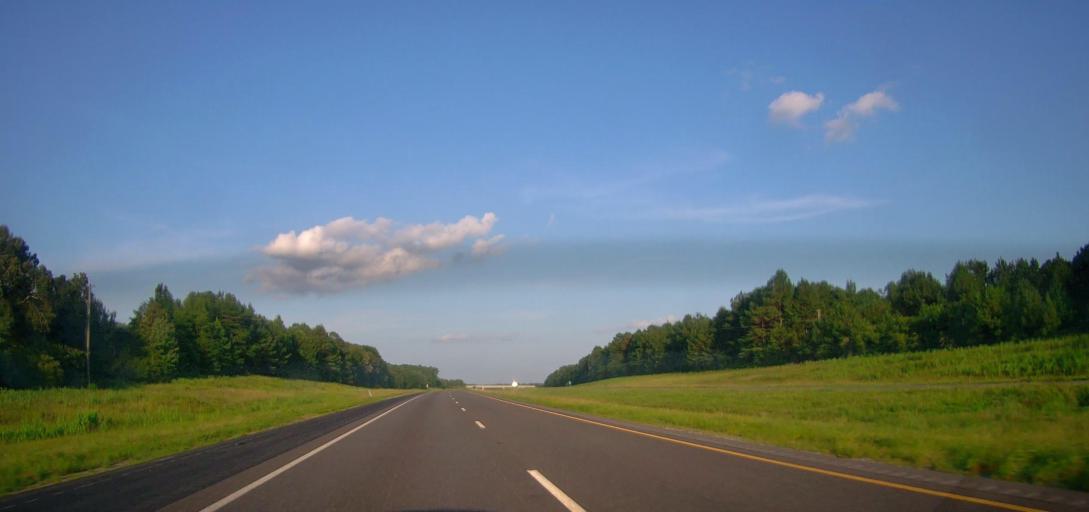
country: US
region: Alabama
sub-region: Walker County
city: Carbon Hill
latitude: 33.9409
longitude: -87.5604
